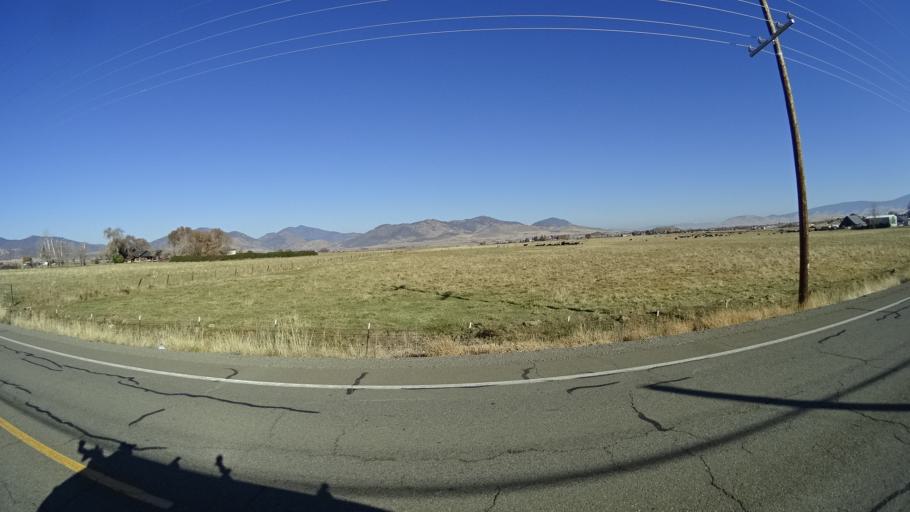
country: US
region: California
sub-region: Siskiyou County
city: Montague
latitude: 41.7053
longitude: -122.5559
